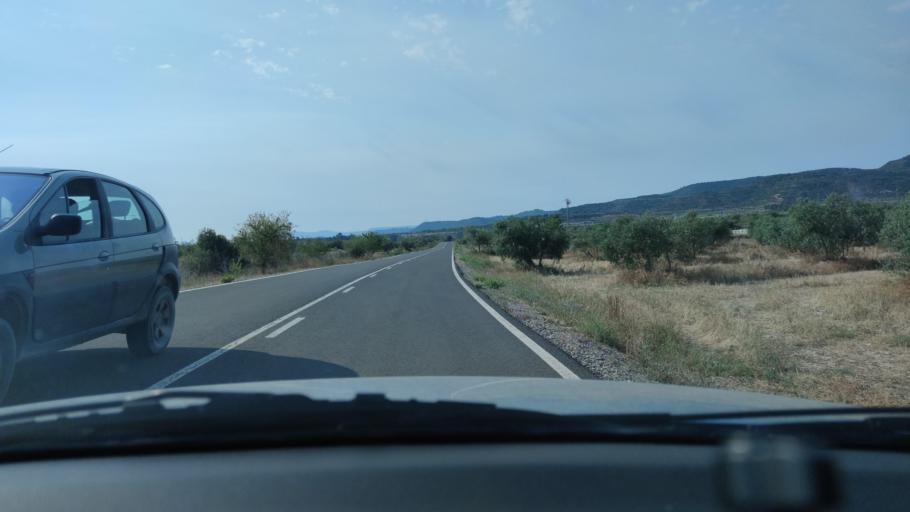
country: ES
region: Catalonia
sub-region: Provincia de Lleida
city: Arbeca
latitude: 41.4890
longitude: 0.8759
